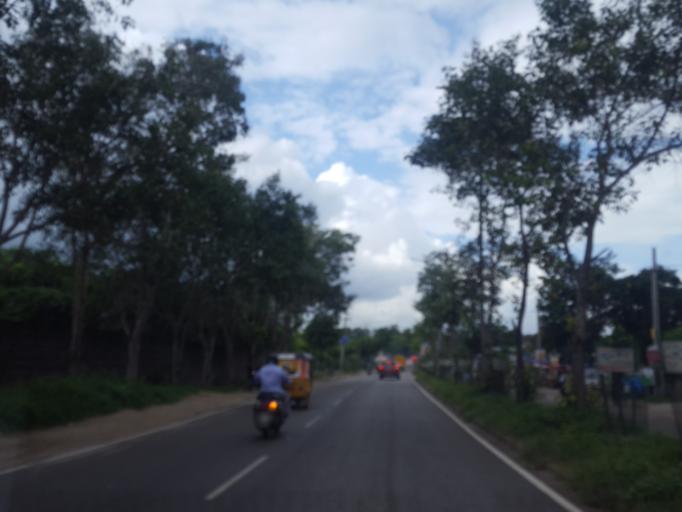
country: IN
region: Telangana
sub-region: Medak
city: Serilingampalle
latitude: 17.4898
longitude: 78.3139
